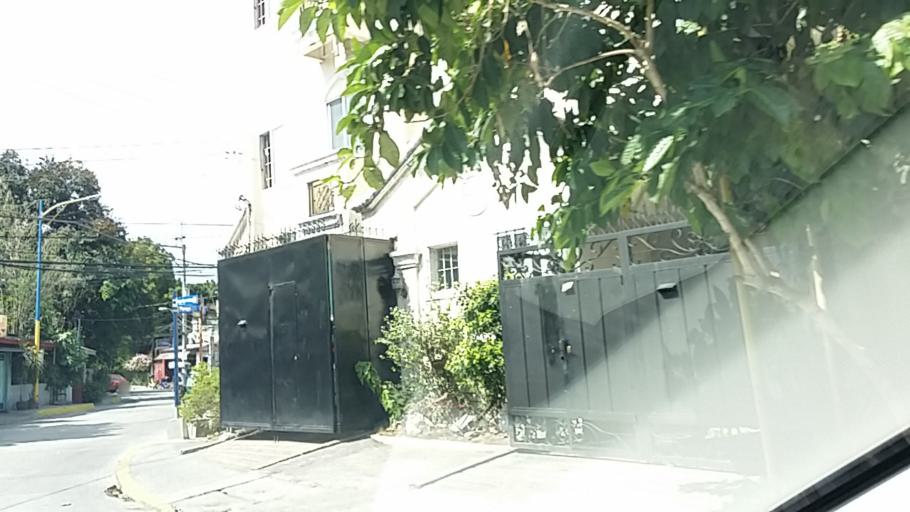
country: PH
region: Metro Manila
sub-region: Mandaluyong
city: Mandaluyong City
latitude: 14.5713
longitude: 121.0354
